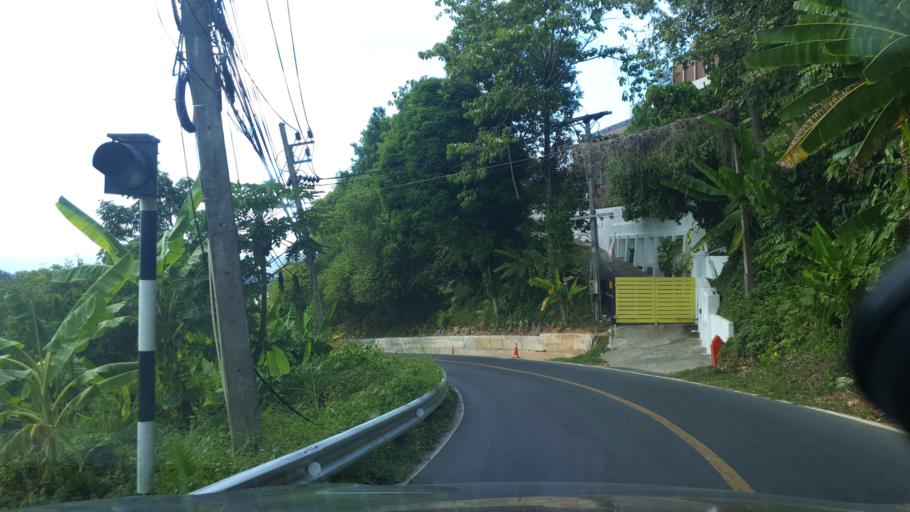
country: TH
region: Phuket
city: Thalang
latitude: 8.0639
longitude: 98.2850
